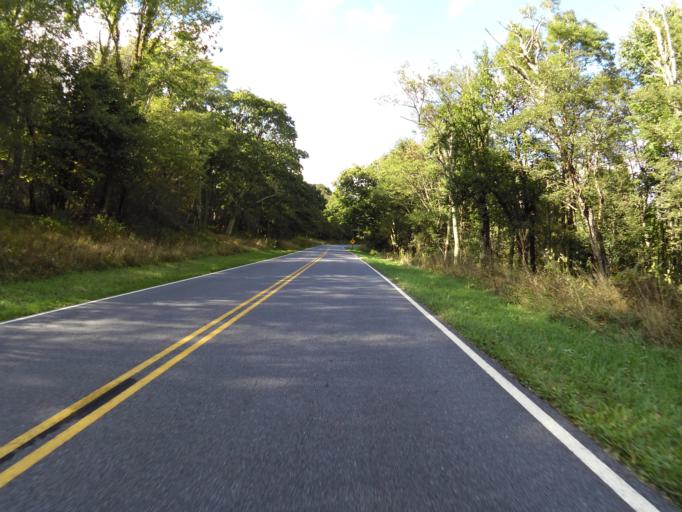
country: US
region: Virginia
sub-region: Page County
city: Luray
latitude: 38.5813
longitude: -78.3831
